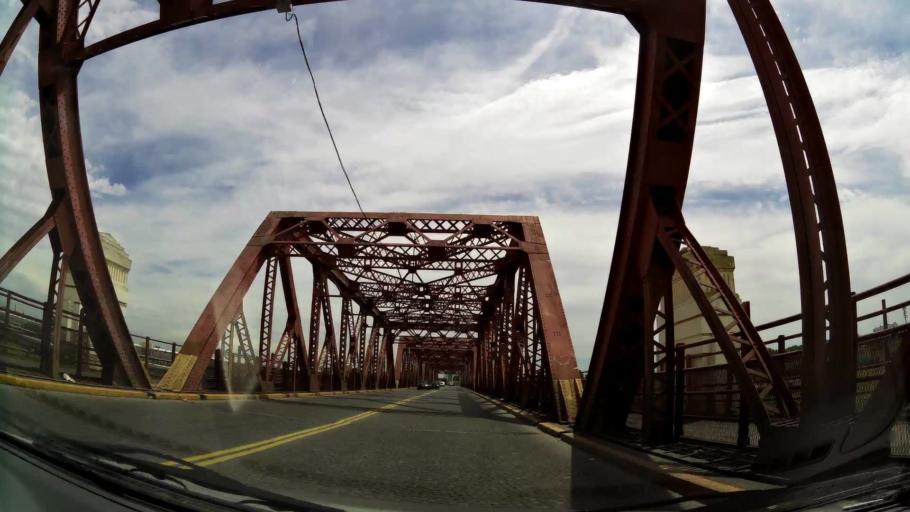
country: AR
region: Buenos Aires
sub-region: Partido de Avellaneda
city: Avellaneda
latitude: -34.6738
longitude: -58.3739
